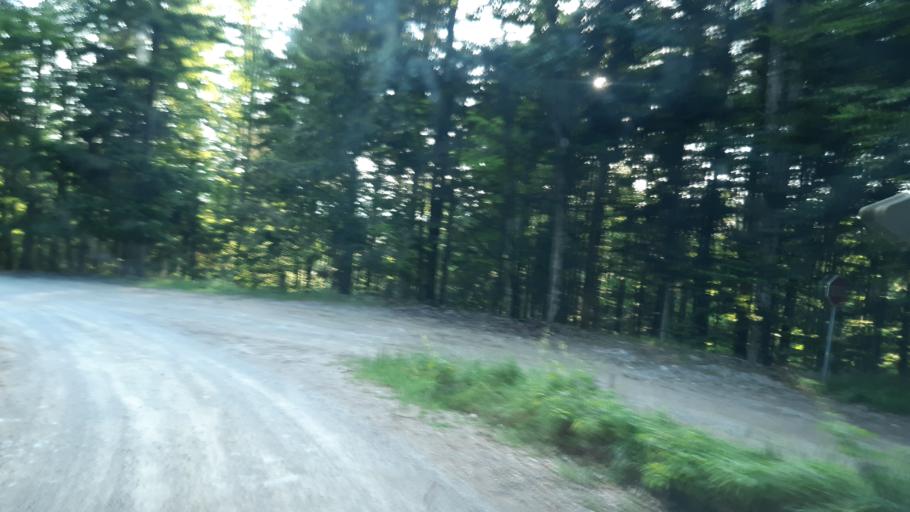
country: SI
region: Kocevje
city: Kocevje
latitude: 45.6762
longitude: 14.9740
